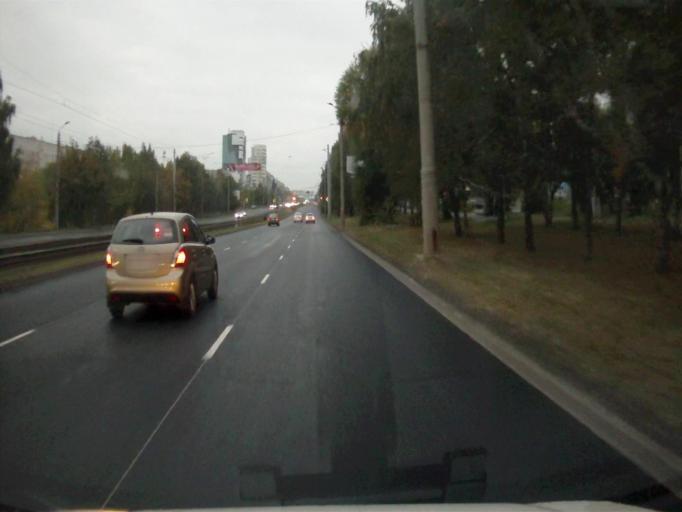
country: RU
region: Chelyabinsk
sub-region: Gorod Chelyabinsk
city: Chelyabinsk
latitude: 55.1891
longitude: 61.3435
